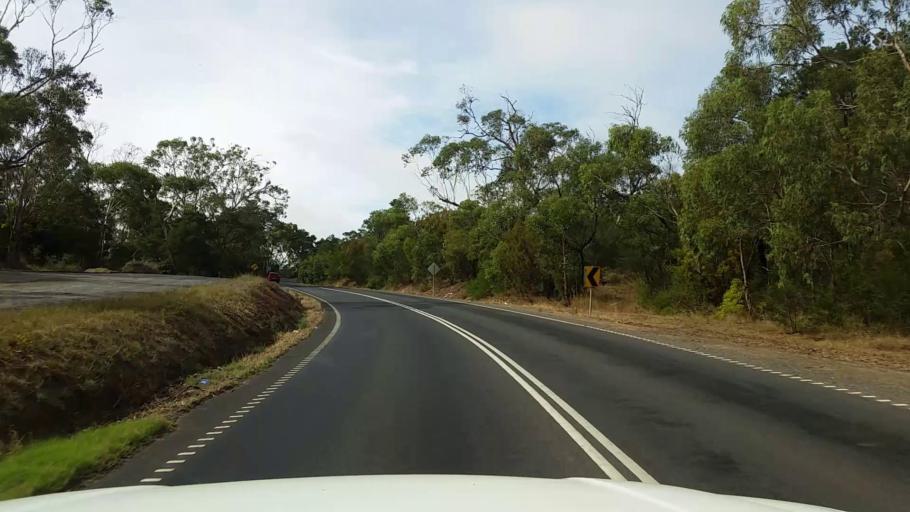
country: AU
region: Victoria
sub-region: Mornington Peninsula
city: Mount Martha
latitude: -38.2878
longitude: 145.0721
